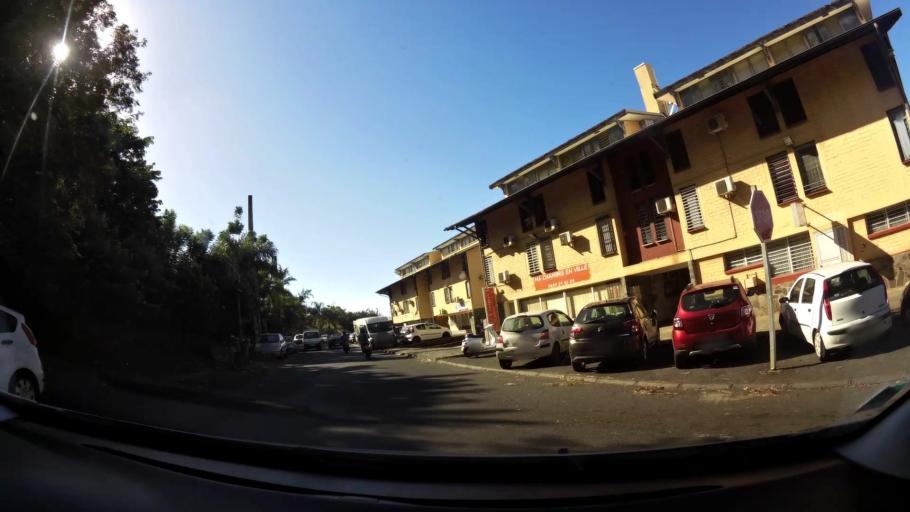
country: YT
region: Mamoudzou
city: Mamoudzou
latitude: -12.7801
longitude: 45.2250
